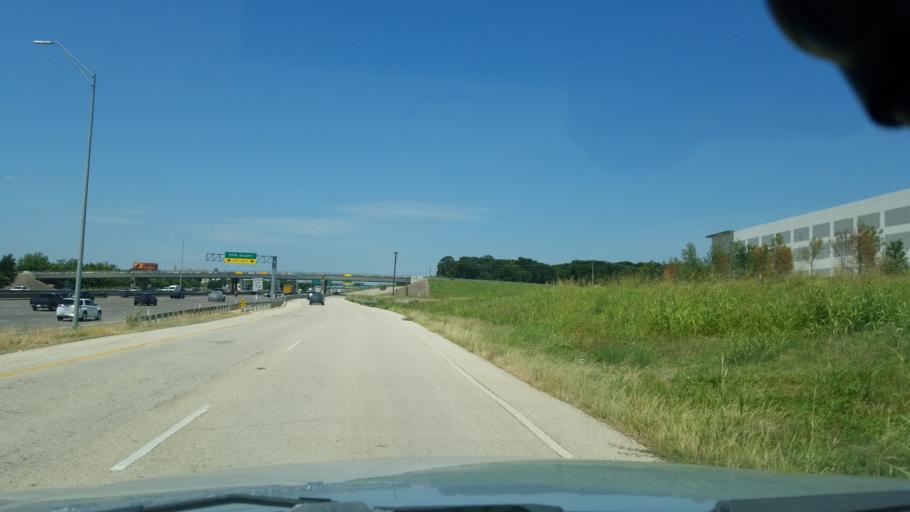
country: US
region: Texas
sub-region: Tarrant County
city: Euless
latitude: 32.8375
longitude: -97.0274
